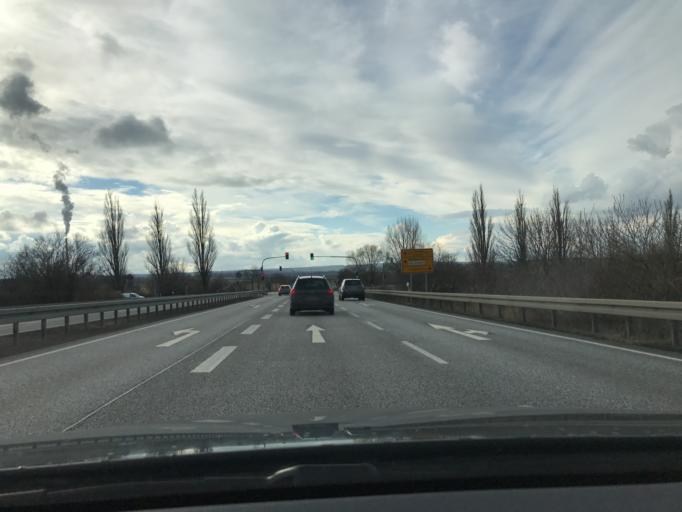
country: DE
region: Saxony-Anhalt
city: Wansleben
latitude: 51.4722
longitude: 11.7499
